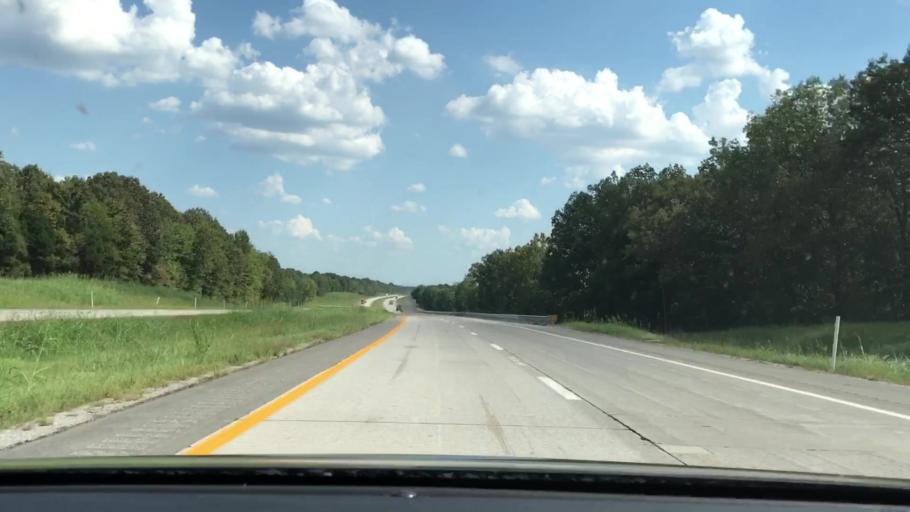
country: US
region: Kentucky
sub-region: Ohio County
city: Oak Grove
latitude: 37.3488
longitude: -86.7821
